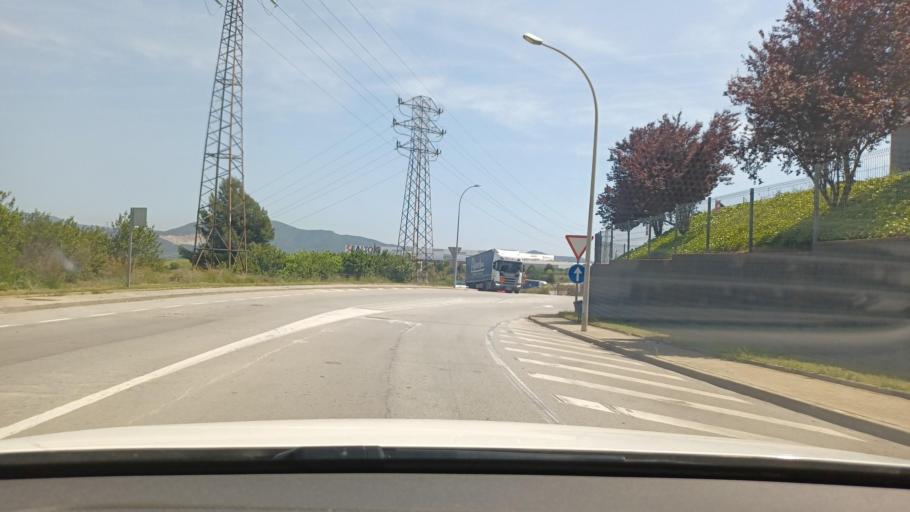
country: ES
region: Catalonia
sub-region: Provincia de Barcelona
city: Ripollet
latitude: 41.5224
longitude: 2.1511
